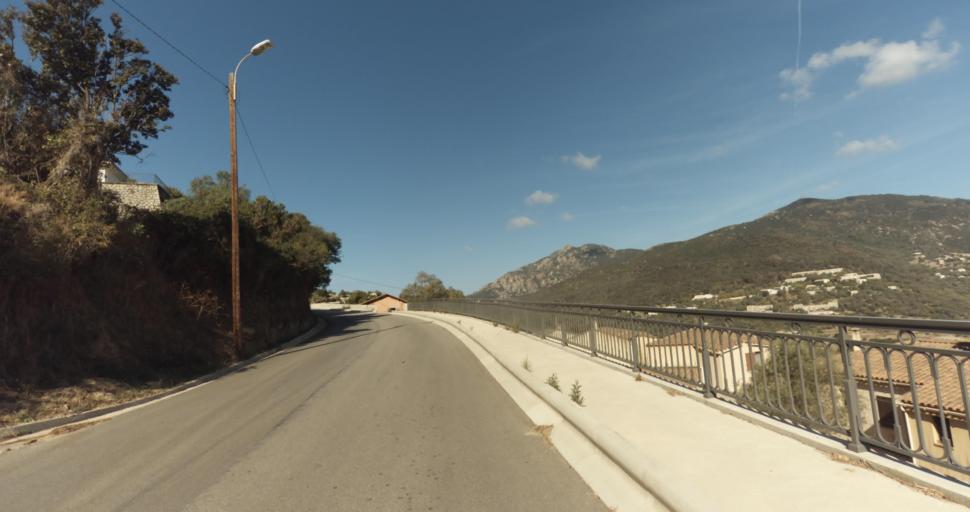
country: FR
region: Corsica
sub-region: Departement de la Corse-du-Sud
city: Ajaccio
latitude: 41.9253
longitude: 8.7249
